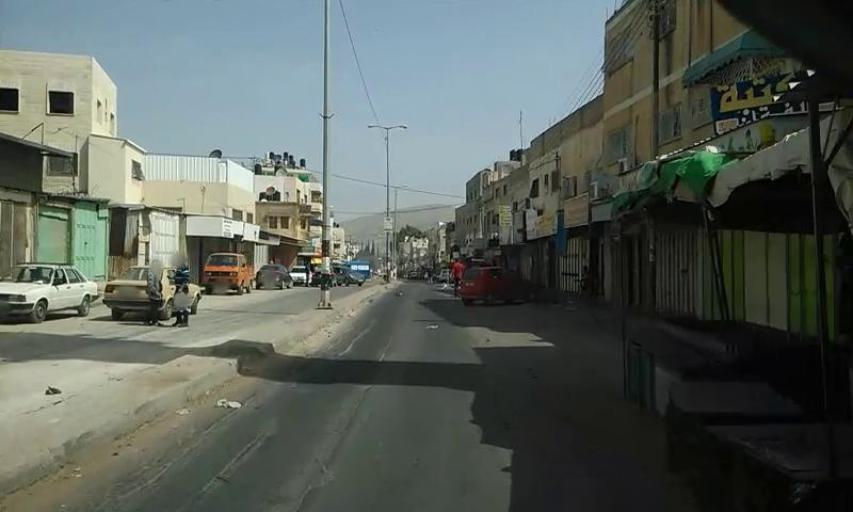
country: PS
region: West Bank
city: `Azmut
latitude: 32.2210
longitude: 35.2968
